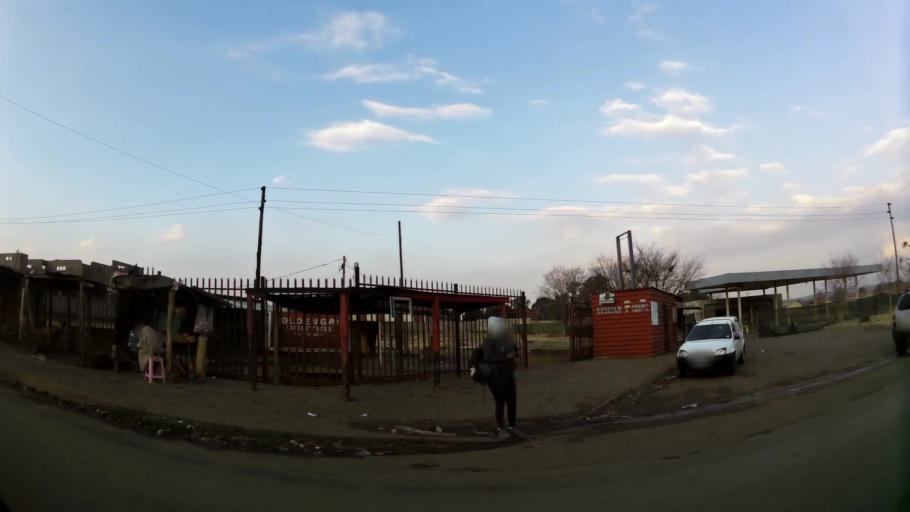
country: ZA
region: Gauteng
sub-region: City of Johannesburg Metropolitan Municipality
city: Orange Farm
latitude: -26.5386
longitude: 27.8323
